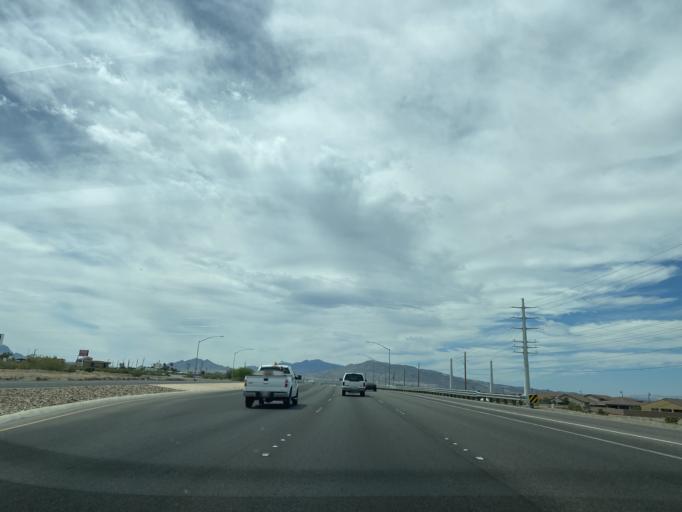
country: US
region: Nevada
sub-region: Clark County
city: Henderson
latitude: 36.0704
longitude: -114.9577
